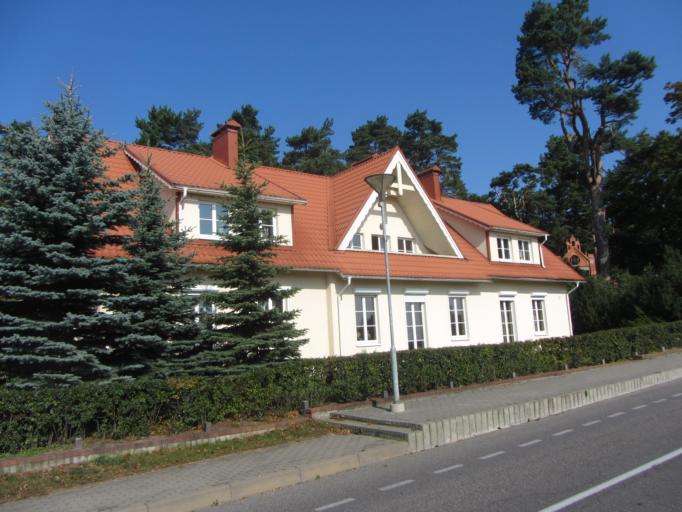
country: LT
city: Nida
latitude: 55.3087
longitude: 21.0077
